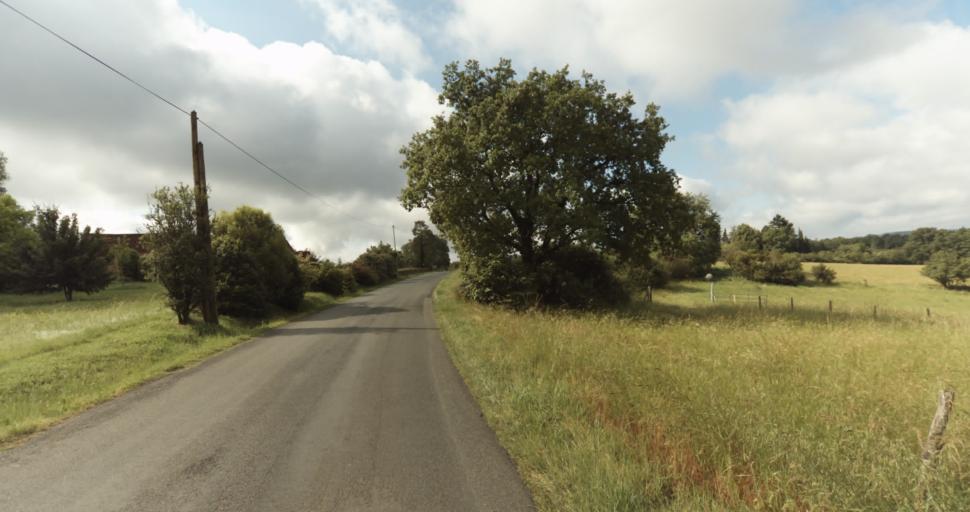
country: FR
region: Aquitaine
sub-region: Departement de la Dordogne
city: Le Bugue
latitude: 44.9257
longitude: 0.8221
